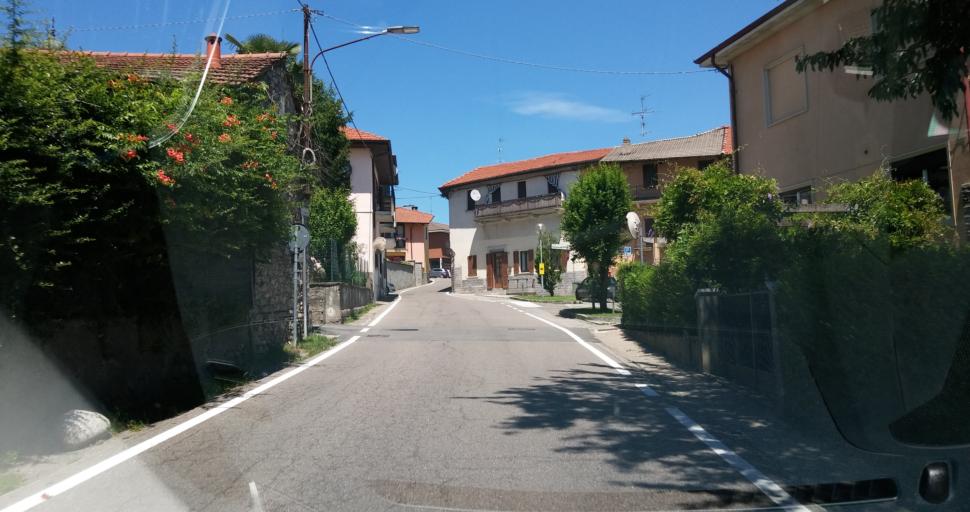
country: IT
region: Lombardy
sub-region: Provincia di Varese
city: Cimbro
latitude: 45.7511
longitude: 8.7283
